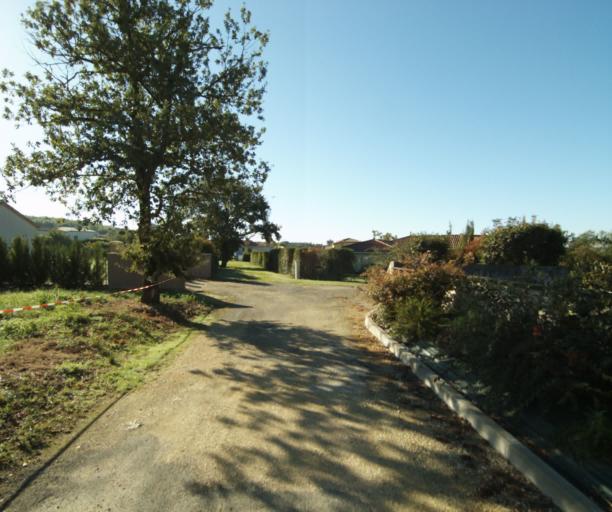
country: FR
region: Midi-Pyrenees
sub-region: Departement du Gers
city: Gondrin
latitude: 43.8389
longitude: 0.2549
